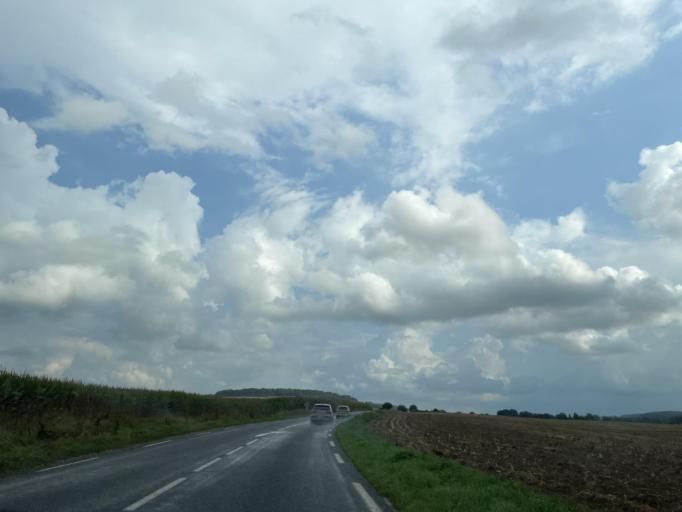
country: FR
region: Haute-Normandie
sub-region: Departement de la Seine-Maritime
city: Envermeu
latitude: 49.8827
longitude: 1.2966
